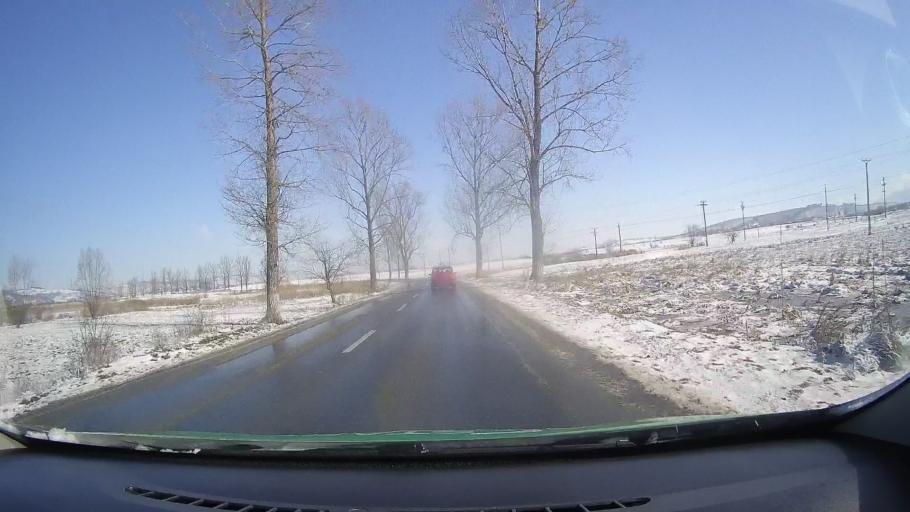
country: RO
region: Sibiu
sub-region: Comuna Avrig
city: Marsa
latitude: 45.7056
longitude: 24.3676
